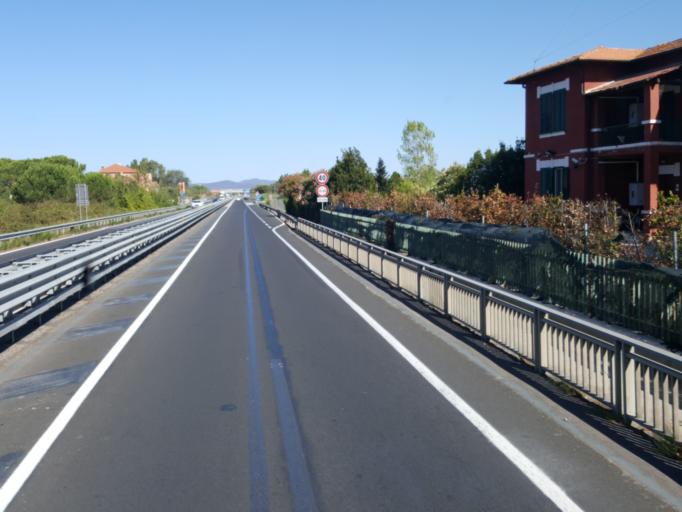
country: IT
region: Tuscany
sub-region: Provincia di Grosseto
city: Albinia
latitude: 42.4963
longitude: 11.2076
